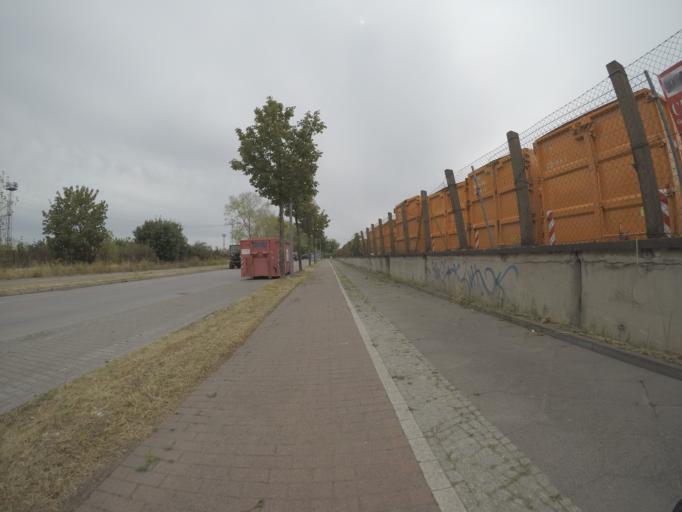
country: DE
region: Berlin
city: Alt-Hohenschoenhausen
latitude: 52.5461
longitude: 13.5254
